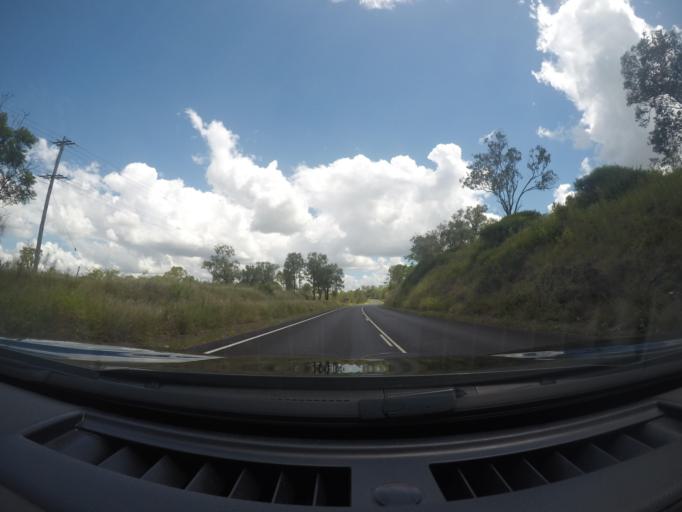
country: AU
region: Queensland
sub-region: Moreton Bay
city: Woodford
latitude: -27.1368
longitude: 152.5545
